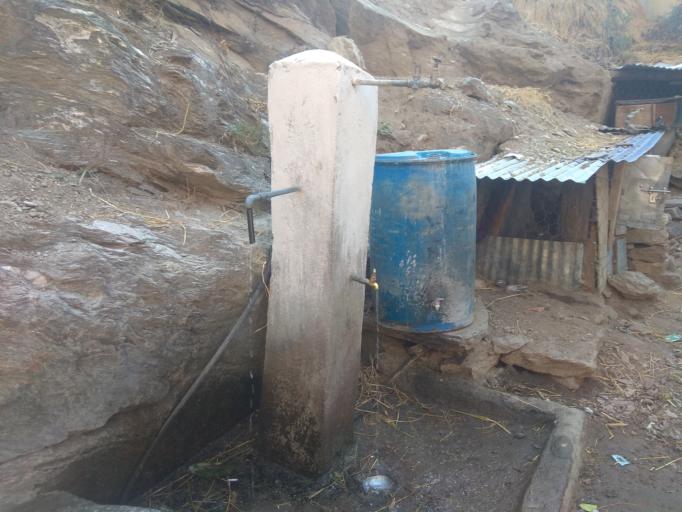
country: NP
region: Mid Western
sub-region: Bheri Zone
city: Dailekh
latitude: 29.2696
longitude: 81.7122
